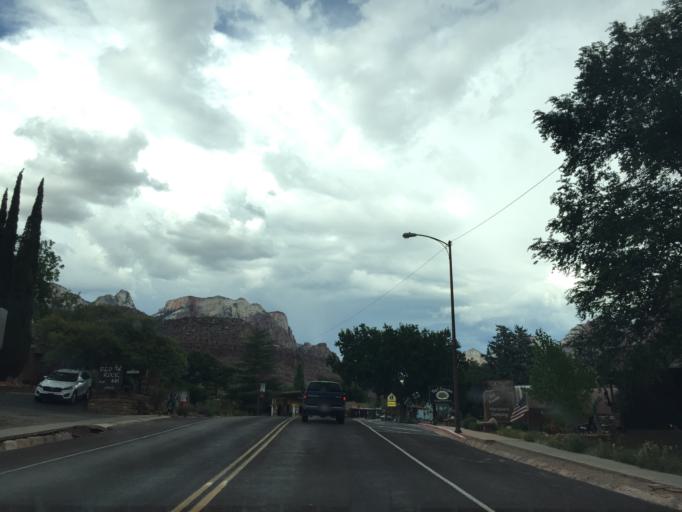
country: US
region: Utah
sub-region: Washington County
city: Hildale
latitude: 37.1877
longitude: -113.0011
